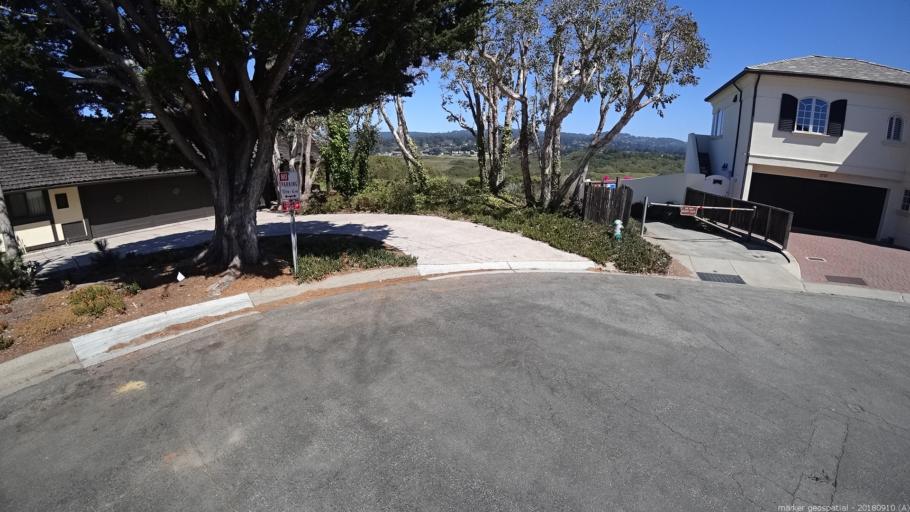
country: US
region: California
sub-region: Monterey County
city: Carmel-by-the-Sea
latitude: 36.5343
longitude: -121.9255
